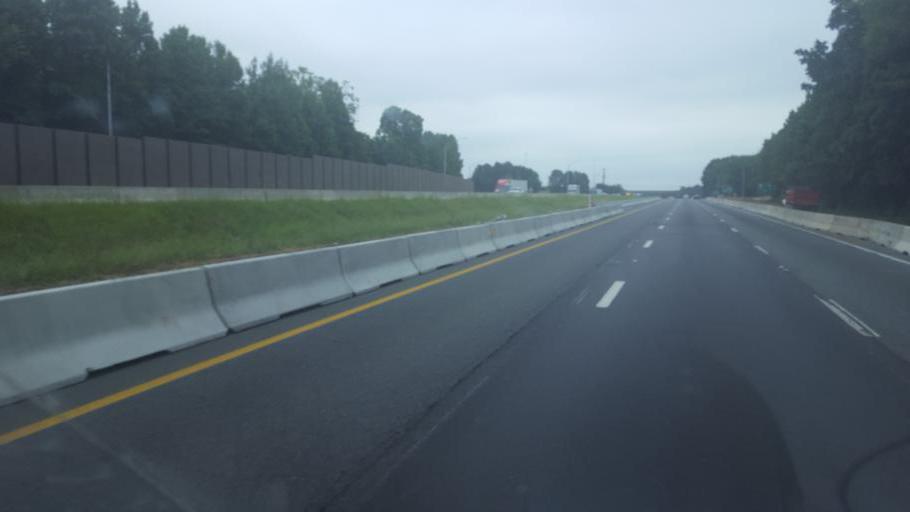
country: US
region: North Carolina
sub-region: Mecklenburg County
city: Charlotte
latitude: 35.3024
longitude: -80.8492
